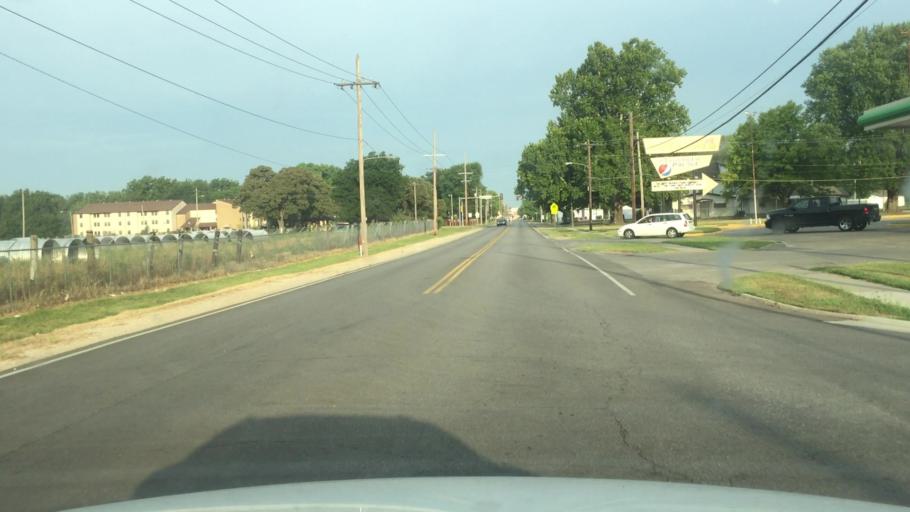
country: US
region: Kansas
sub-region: Shawnee County
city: Topeka
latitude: 39.0589
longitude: -95.6389
